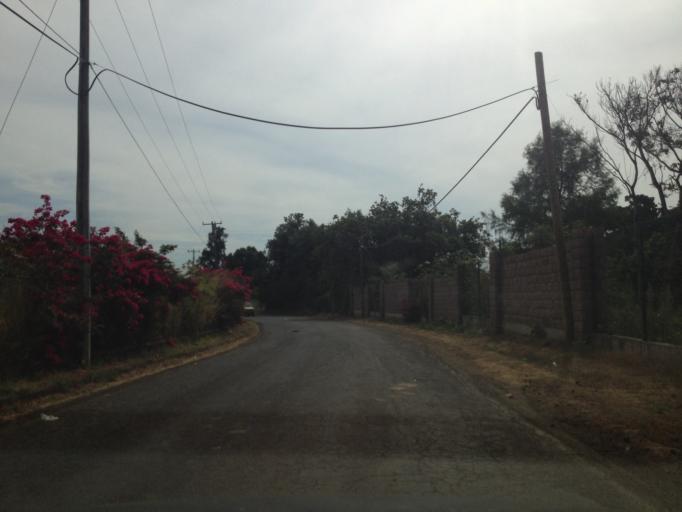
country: MX
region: Michoacan
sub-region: Ziracuaretiro
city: Patuan
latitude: 19.4299
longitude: -101.9241
